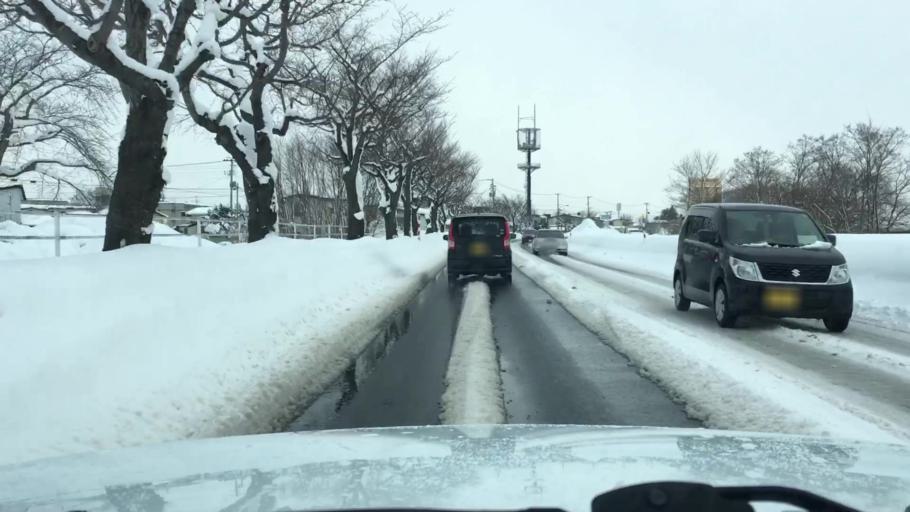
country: JP
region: Aomori
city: Hirosaki
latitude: 40.6119
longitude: 140.4547
